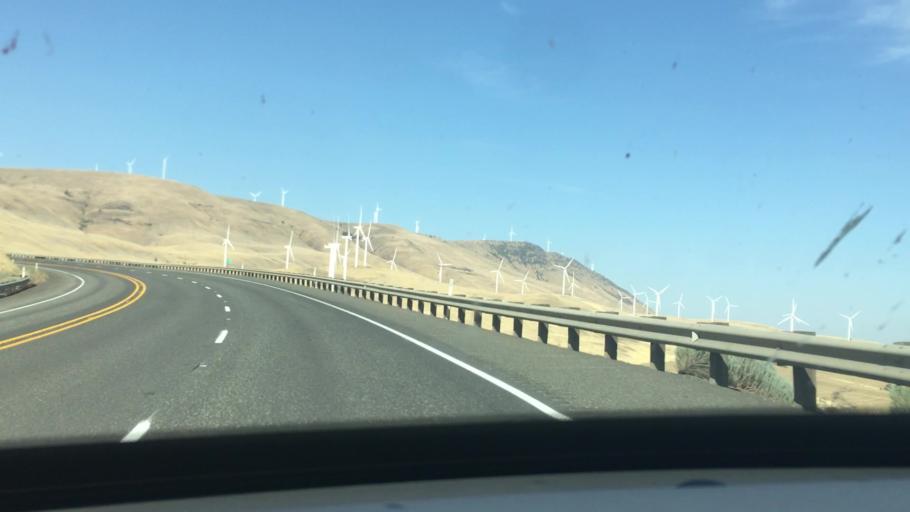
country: US
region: Washington
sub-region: Klickitat County
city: Goldendale
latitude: 45.7097
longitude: -120.8019
